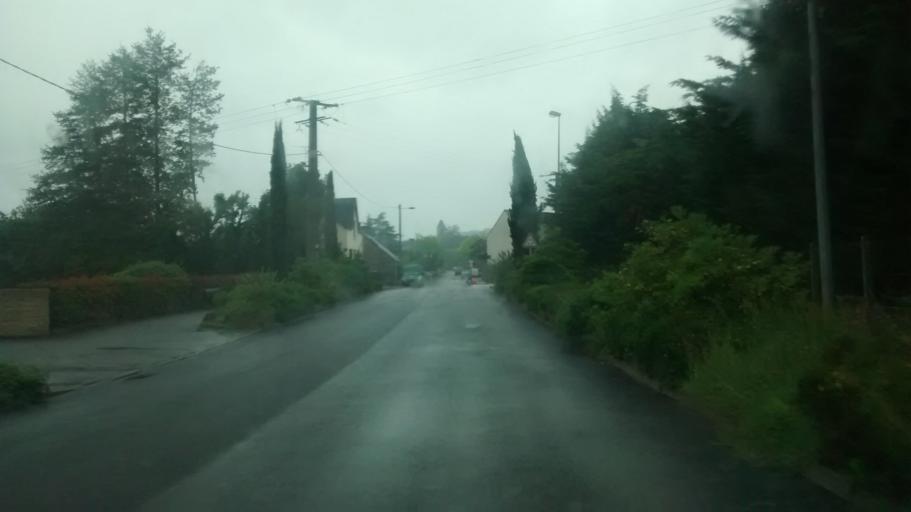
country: FR
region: Brittany
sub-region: Departement du Morbihan
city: La Gacilly
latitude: 47.7668
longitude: -2.1371
